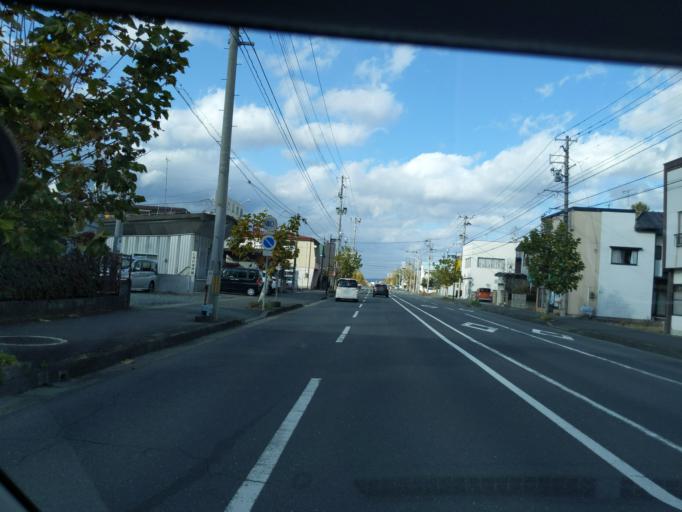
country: JP
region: Iwate
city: Mizusawa
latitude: 39.1374
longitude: 141.1552
